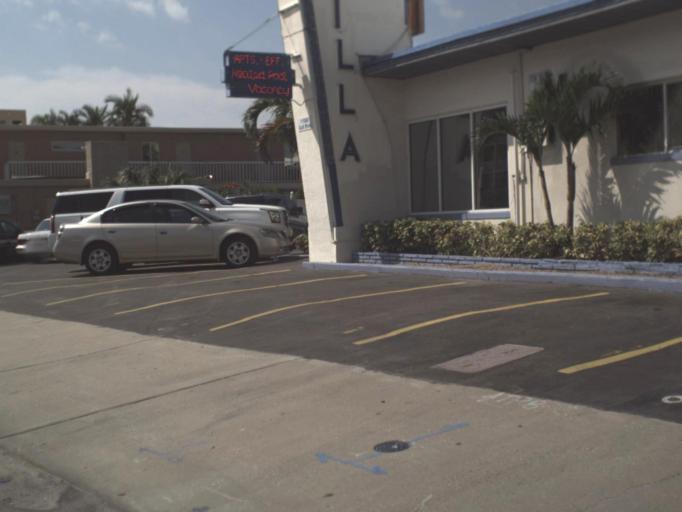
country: US
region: Florida
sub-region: Pinellas County
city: Treasure Island
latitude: 27.7742
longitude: -82.7746
